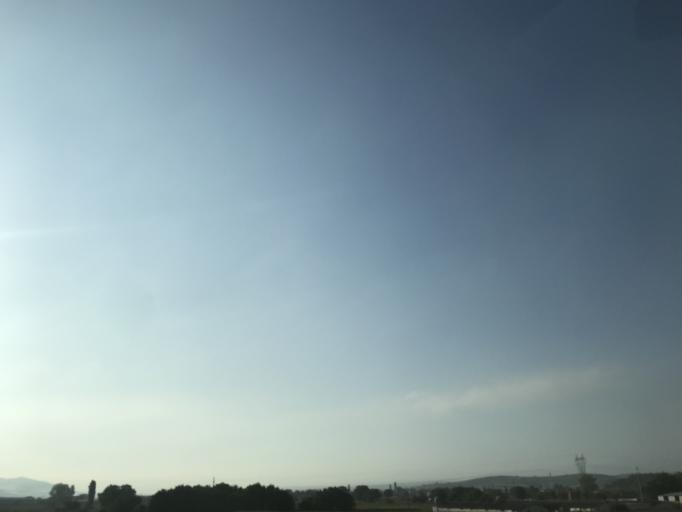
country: TR
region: Balikesir
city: Gobel
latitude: 40.0597
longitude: 28.2402
